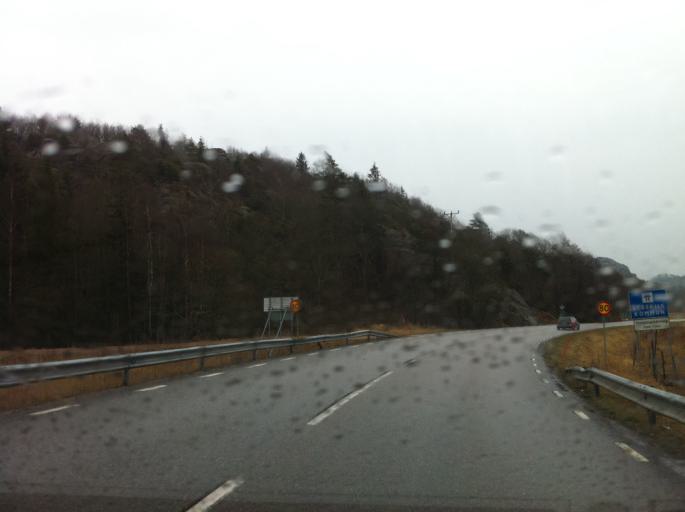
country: SE
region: Vaestra Goetaland
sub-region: Lysekils Kommun
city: Brastad
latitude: 58.4611
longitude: 11.4546
